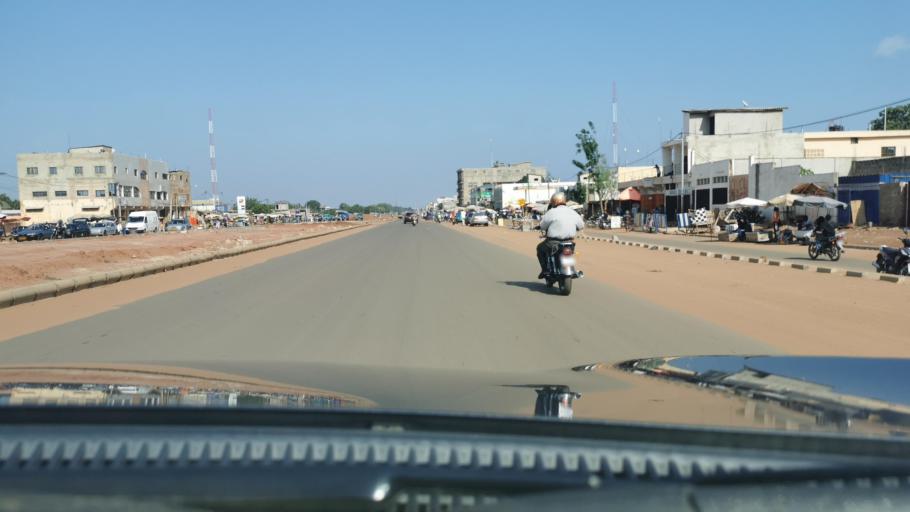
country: TG
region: Maritime
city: Lome
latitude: 6.2020
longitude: 1.1468
